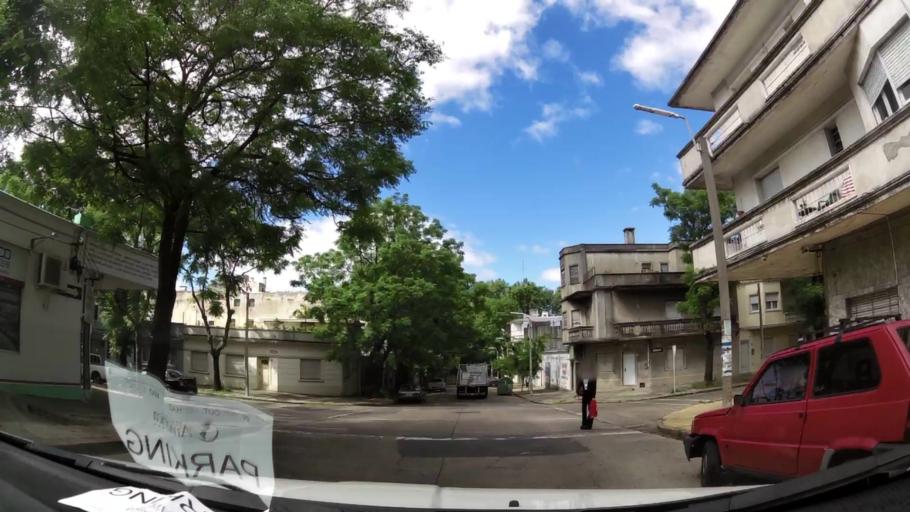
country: UY
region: Montevideo
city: Montevideo
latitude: -34.8795
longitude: -56.1821
